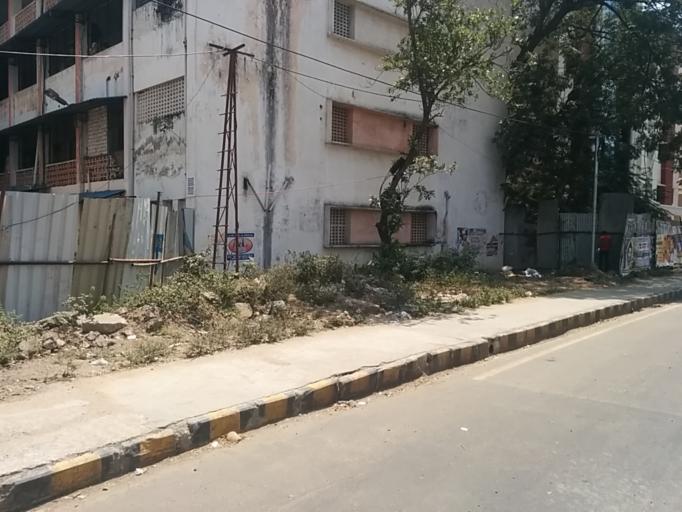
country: IN
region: Tamil Nadu
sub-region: Chennai
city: Chetput
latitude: 13.0462
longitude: 80.2486
